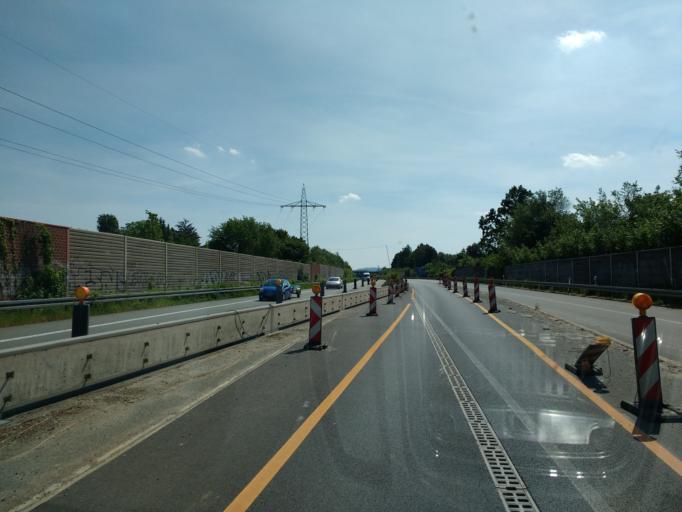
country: DE
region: Lower Saxony
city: Belm
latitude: 52.2811
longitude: 8.1075
